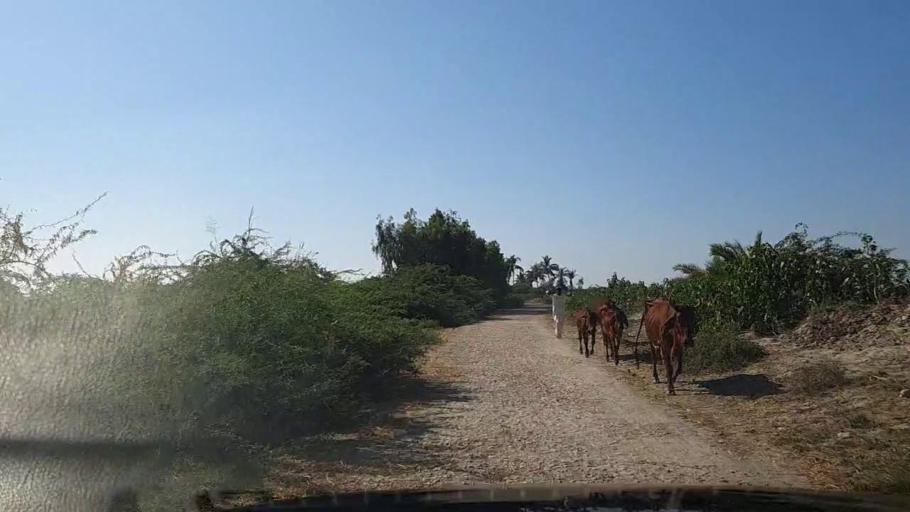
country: PK
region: Sindh
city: Thatta
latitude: 24.7128
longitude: 67.9191
